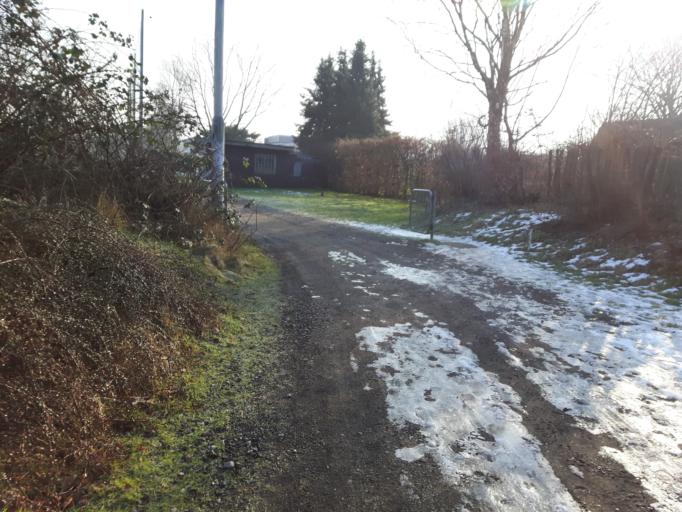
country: DE
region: Schleswig-Holstein
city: Neumunster
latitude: 54.0814
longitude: 10.0011
